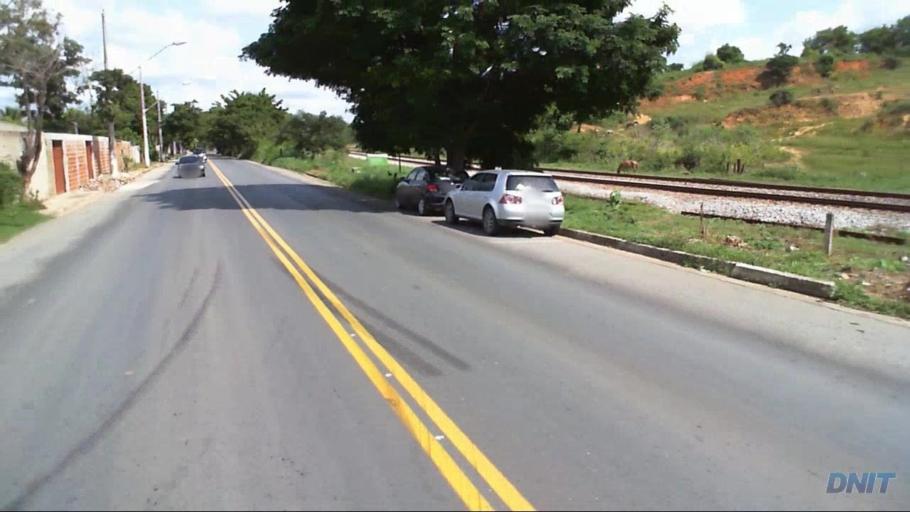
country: BR
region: Minas Gerais
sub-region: Governador Valadares
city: Governador Valadares
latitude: -18.9119
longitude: -41.9965
